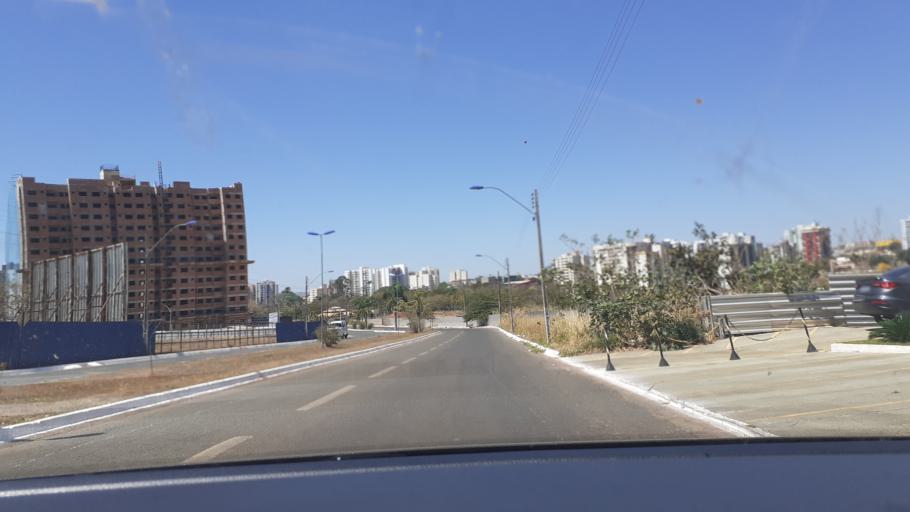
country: BR
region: Goias
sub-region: Caldas Novas
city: Caldas Novas
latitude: -17.7410
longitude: -48.6366
